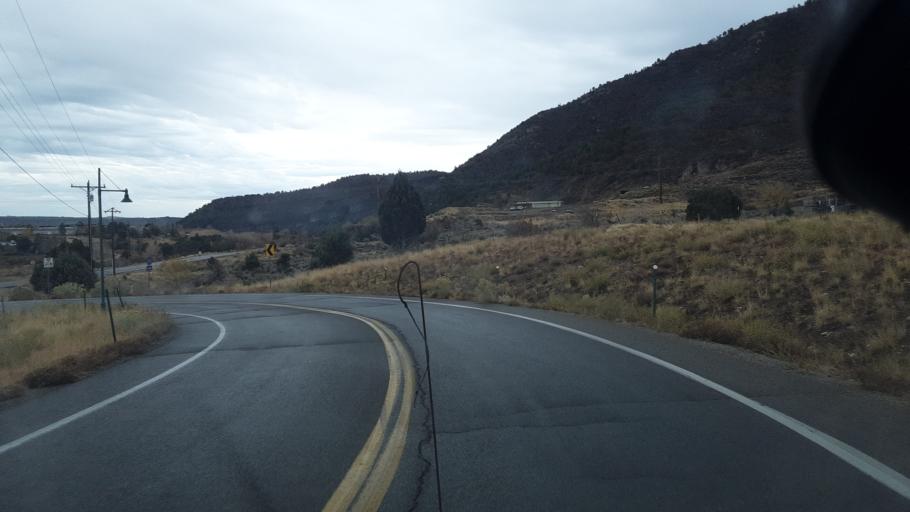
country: US
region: Colorado
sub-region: La Plata County
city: Durango
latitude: 37.2364
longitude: -107.8703
